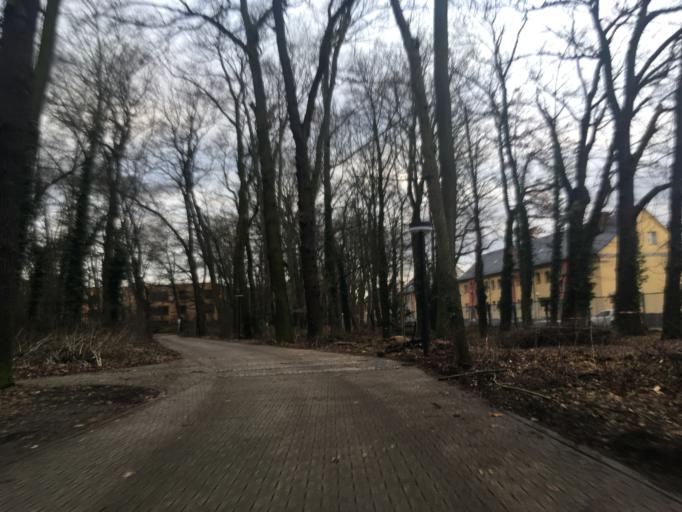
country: DE
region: Berlin
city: Wittenau
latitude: 52.5829
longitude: 13.3252
